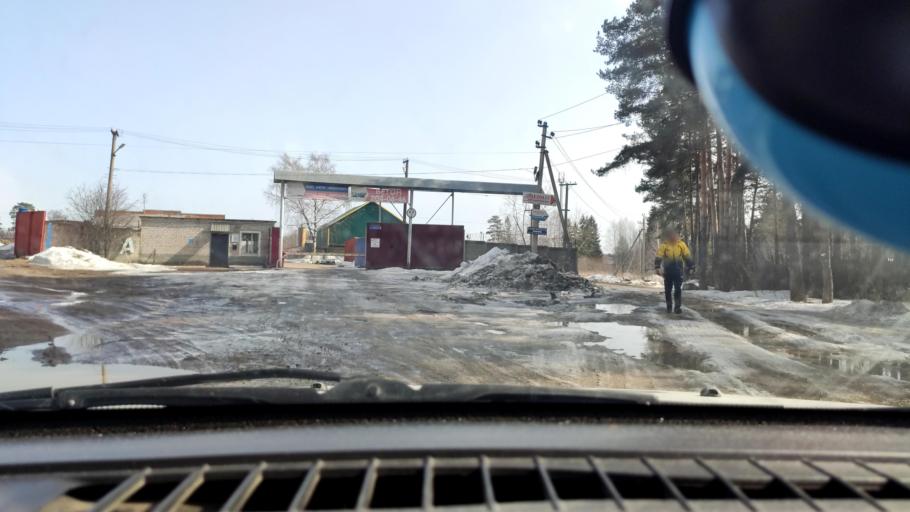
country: RU
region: Perm
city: Kondratovo
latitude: 58.0384
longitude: 56.0617
